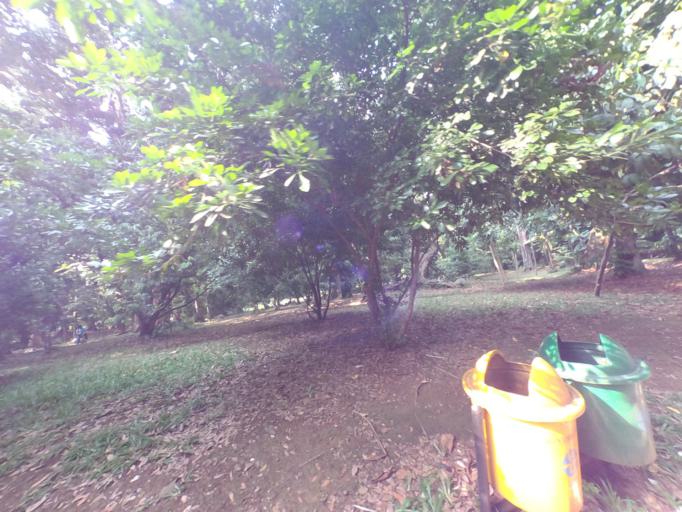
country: ID
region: West Java
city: Bogor
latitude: -6.6018
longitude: 106.7990
